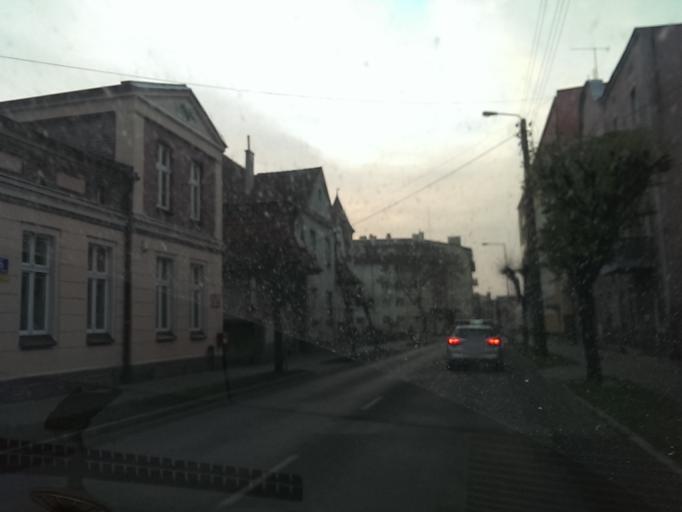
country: PL
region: Kujawsko-Pomorskie
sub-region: Powiat nakielski
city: Naklo nad Notecia
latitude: 53.1391
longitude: 17.6046
